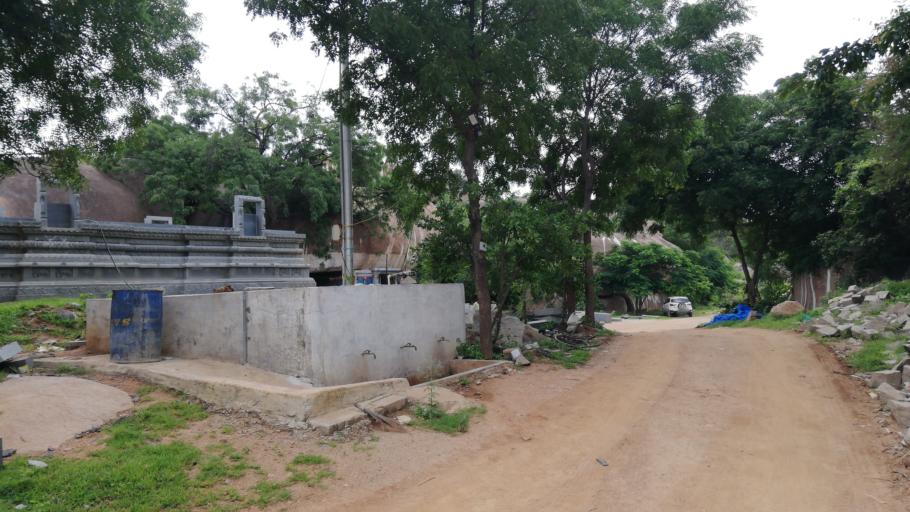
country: IN
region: Telangana
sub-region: Rangareddi
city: Kukatpalli
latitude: 17.4097
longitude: 78.3627
